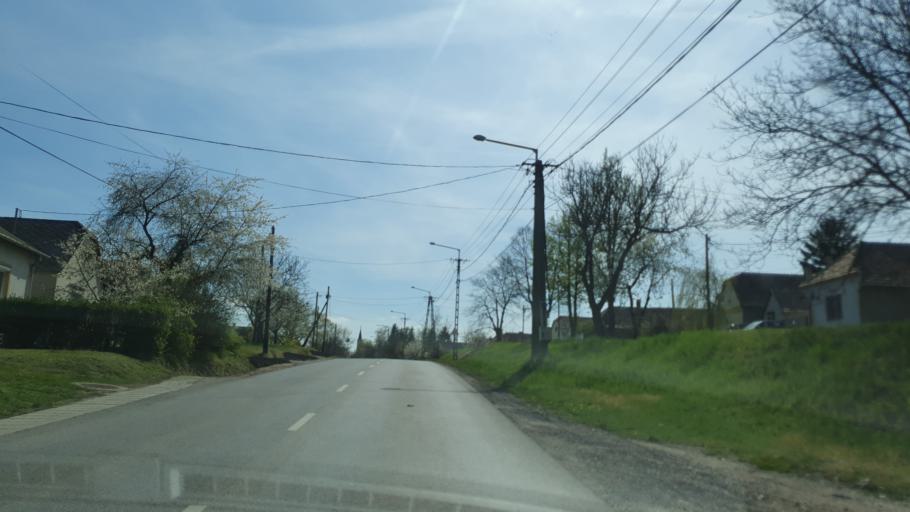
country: HU
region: Fejer
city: Pusztavam
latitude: 47.4360
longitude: 18.2319
